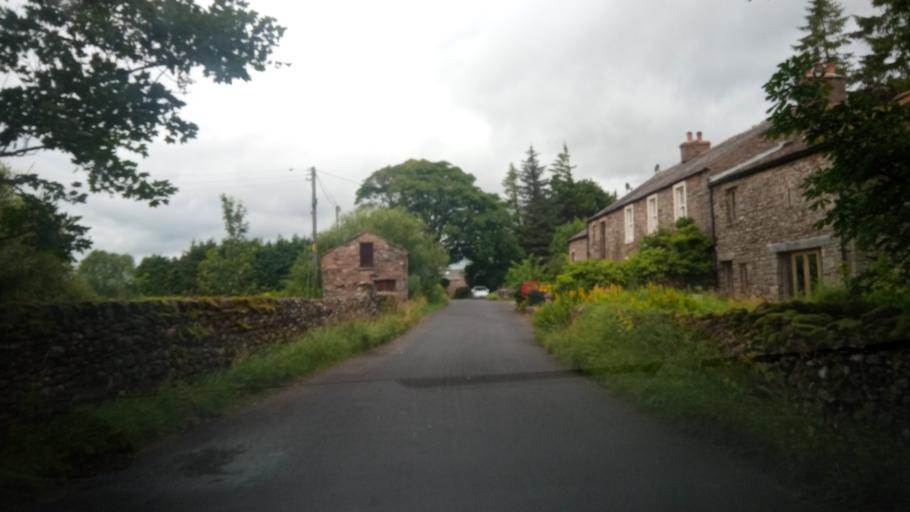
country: GB
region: England
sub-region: Cumbria
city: Kirkby Stephen
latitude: 54.4080
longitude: -2.3369
